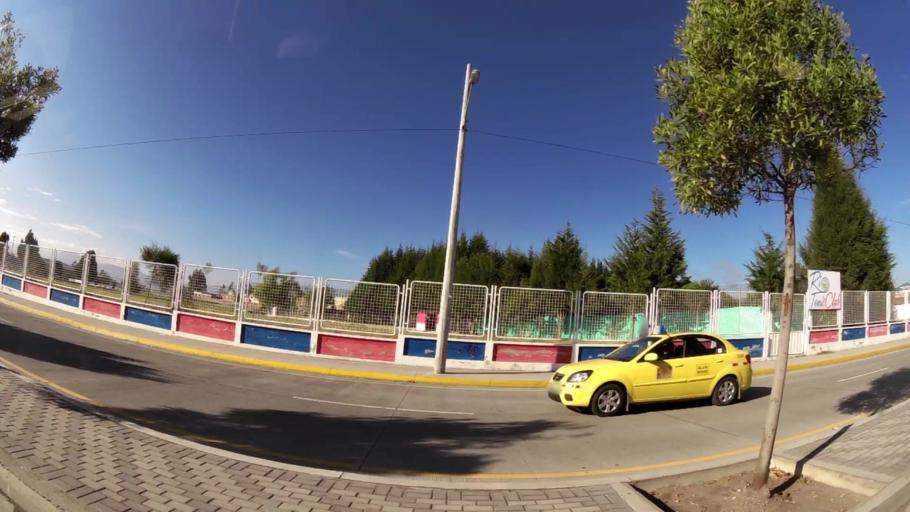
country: EC
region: Chimborazo
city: Riobamba
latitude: -1.6868
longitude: -78.6413
